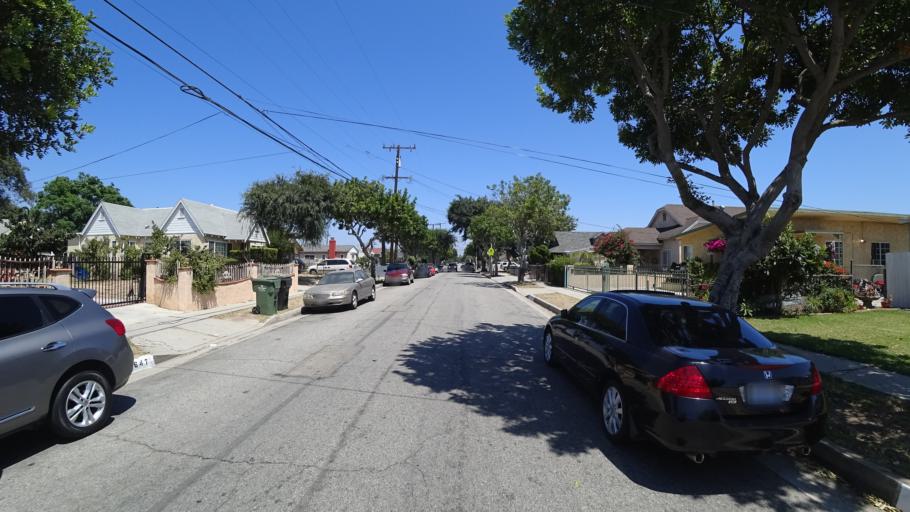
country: US
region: California
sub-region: Los Angeles County
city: Lennox
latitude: 33.9377
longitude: -118.3366
